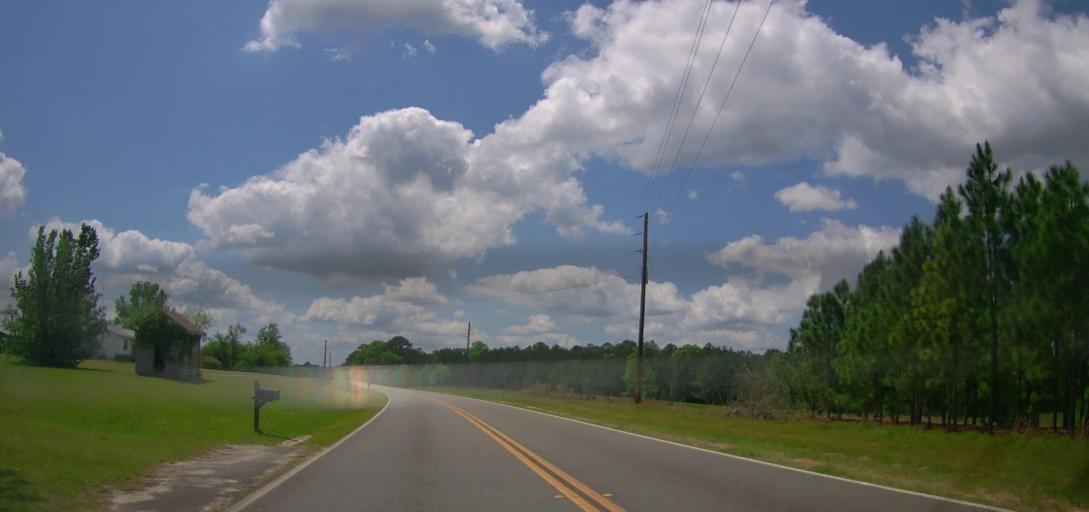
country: US
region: Georgia
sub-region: Laurens County
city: East Dublin
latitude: 32.5279
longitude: -82.7085
